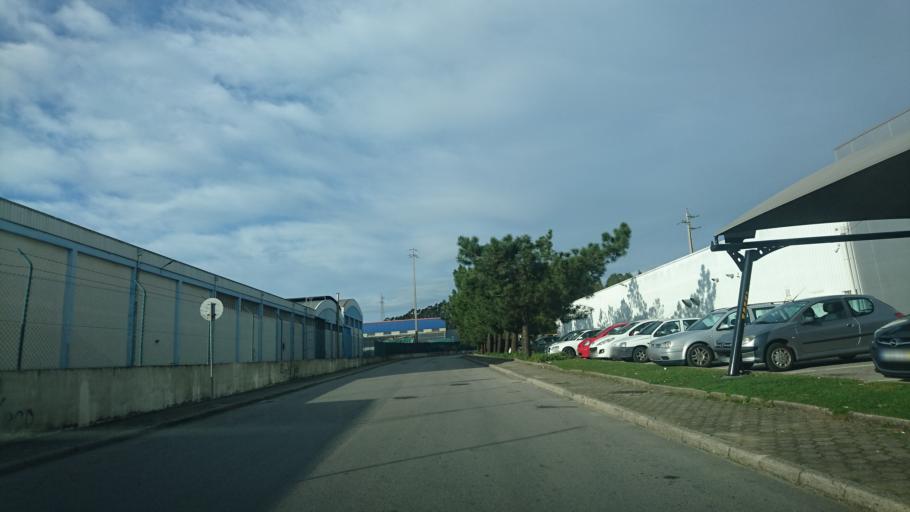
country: PT
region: Aveiro
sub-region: Ovar
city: Cortegaca
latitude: 40.9622
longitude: -8.6104
